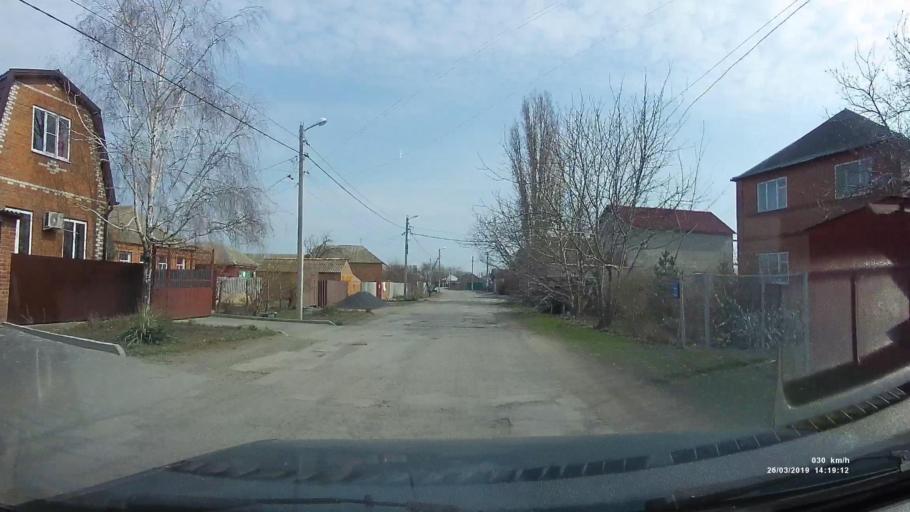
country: RU
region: Rostov
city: Novobessergenovka
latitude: 47.1897
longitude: 38.8682
